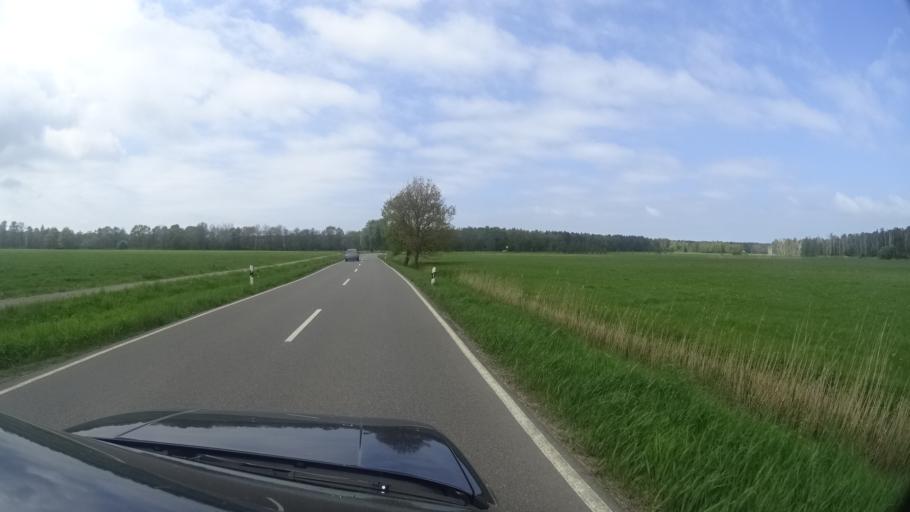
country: DE
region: Mecklenburg-Vorpommern
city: Ostseebad Dierhagen
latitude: 54.2771
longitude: 12.3242
